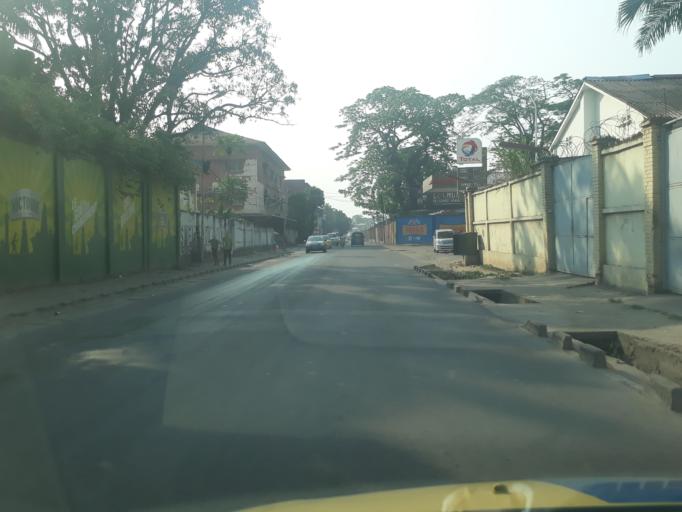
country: CD
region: Kinshasa
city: Kinshasa
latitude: -4.3107
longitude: 15.3290
